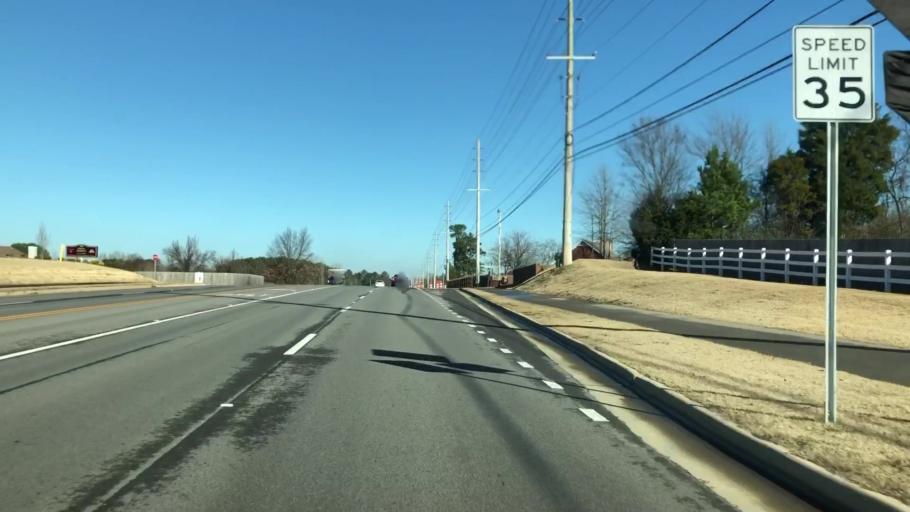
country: US
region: Alabama
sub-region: Madison County
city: Madison
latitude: 34.7413
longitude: -86.7861
